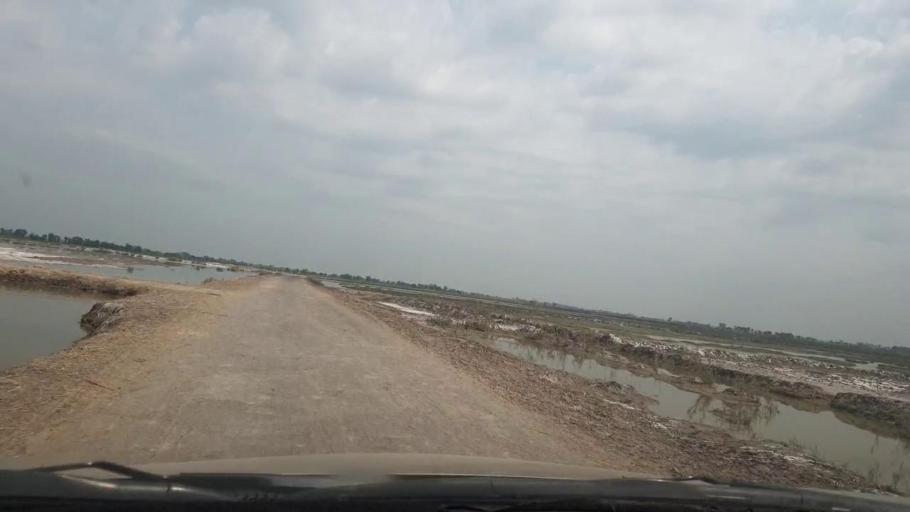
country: PK
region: Sindh
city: Ratodero
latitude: 27.7075
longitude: 68.2287
